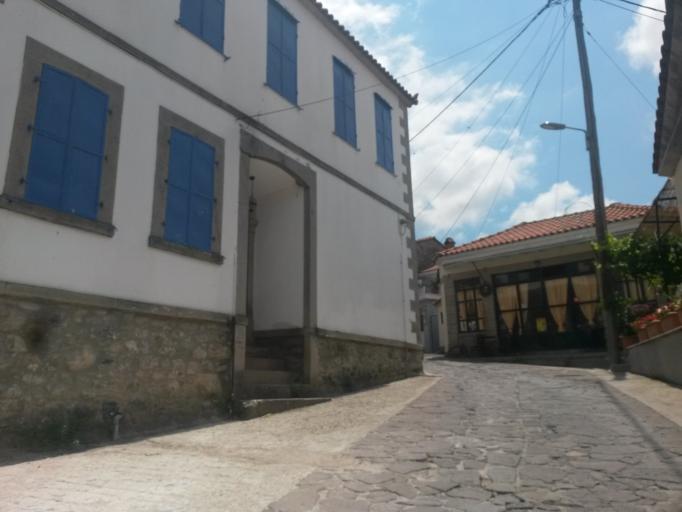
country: GR
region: North Aegean
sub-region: Nomos Lesvou
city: Petra
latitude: 39.2599
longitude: 26.0744
